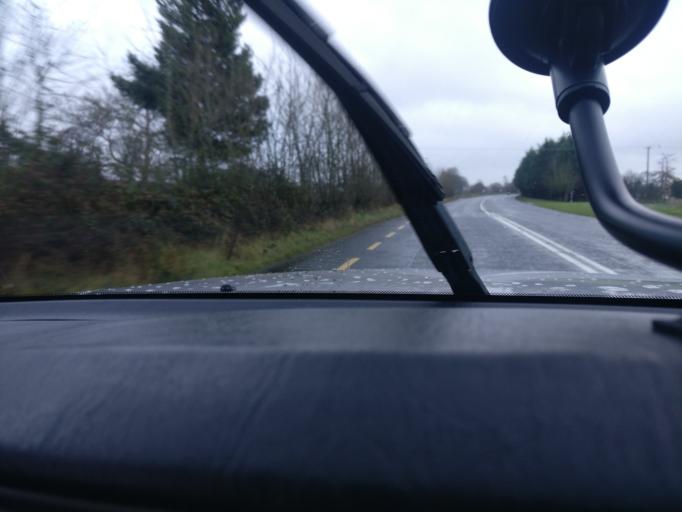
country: IE
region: Leinster
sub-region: An Mhi
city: Longwood
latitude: 53.4301
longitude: -6.9235
